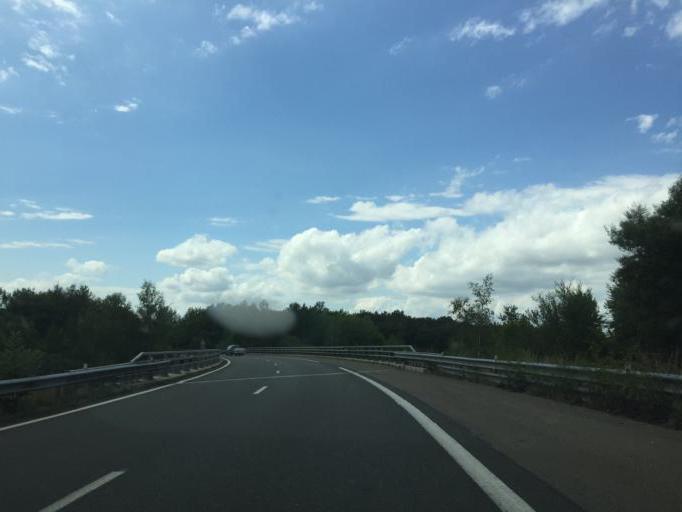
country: FR
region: Rhone-Alpes
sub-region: Departement de l'Ain
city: Viriat
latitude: 46.2552
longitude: 5.2517
